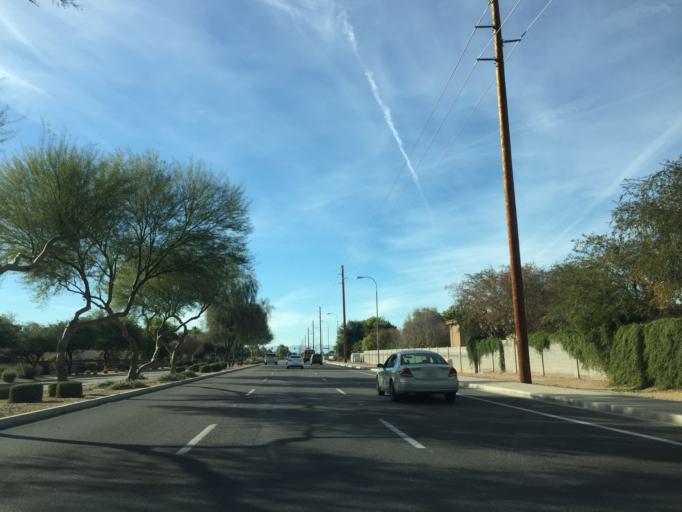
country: US
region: Arizona
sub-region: Maricopa County
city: Sun Lakes
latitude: 33.2192
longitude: -111.7942
